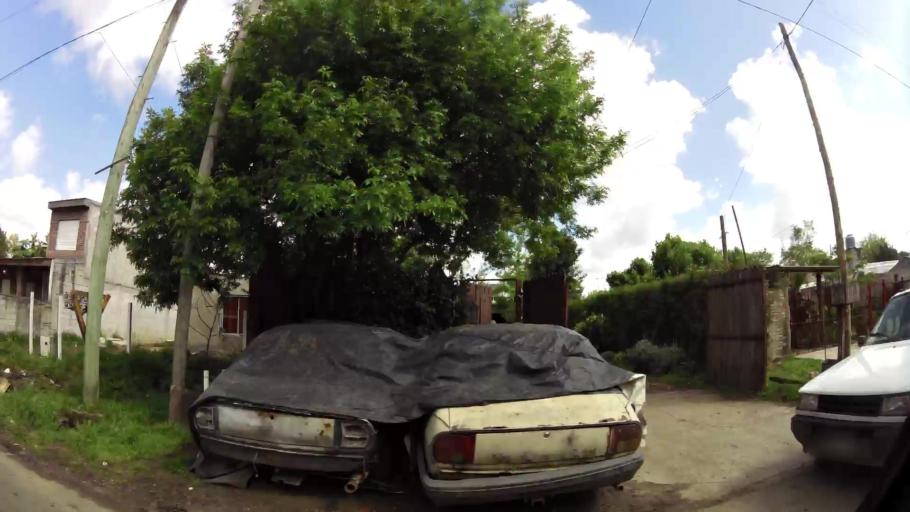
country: AR
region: Buenos Aires
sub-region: Partido de Quilmes
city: Quilmes
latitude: -34.8301
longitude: -58.1717
